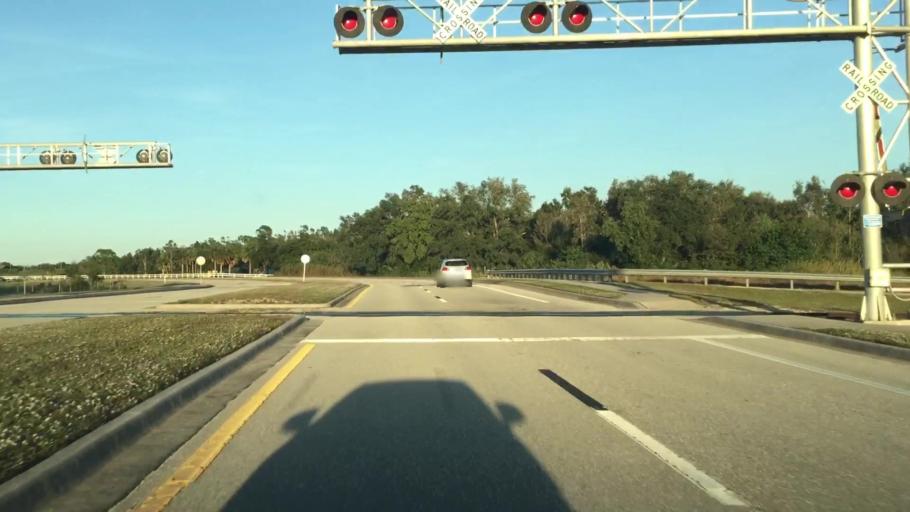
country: US
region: Florida
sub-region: Lee County
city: Estero
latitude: 26.4232
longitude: -81.8056
